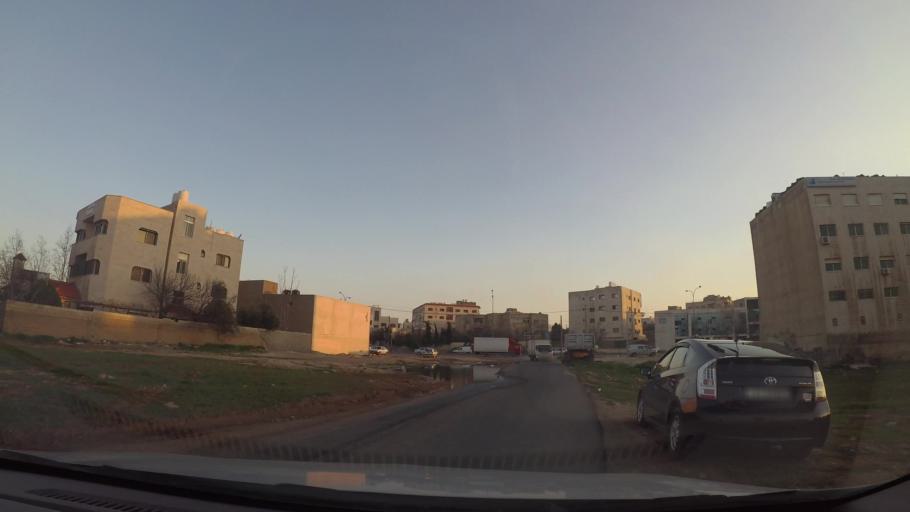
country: JO
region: Amman
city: Al Quwaysimah
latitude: 31.9010
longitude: 35.9317
